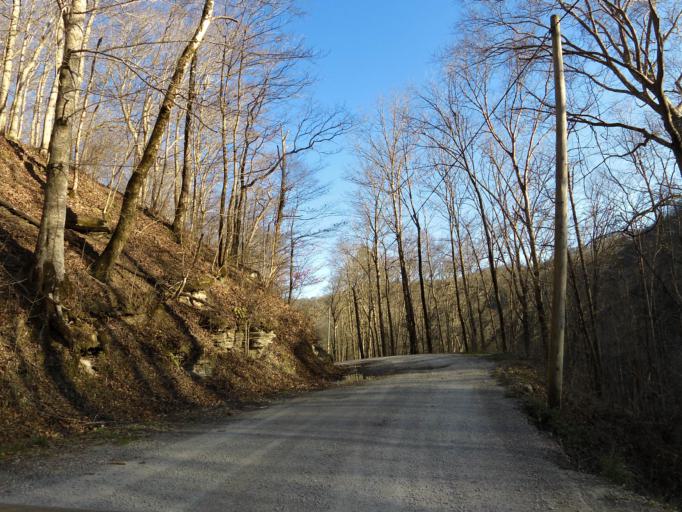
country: US
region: Tennessee
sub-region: Campbell County
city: Caryville
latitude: 36.2580
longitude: -84.3502
